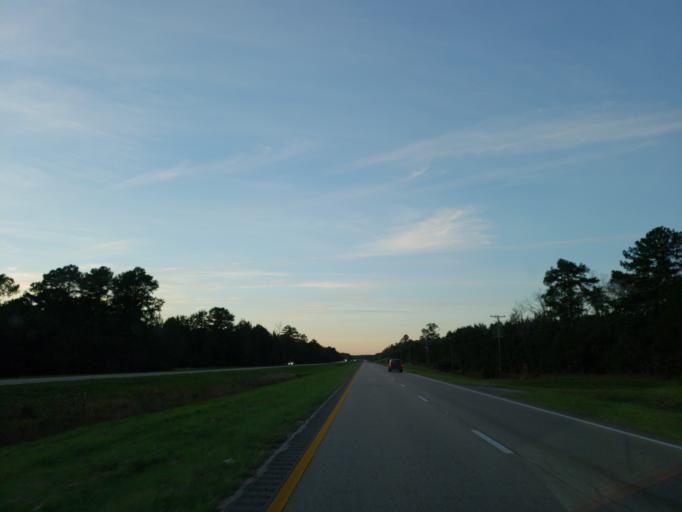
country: US
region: Mississippi
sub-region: Wayne County
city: Belmont
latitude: 31.5833
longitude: -88.5431
